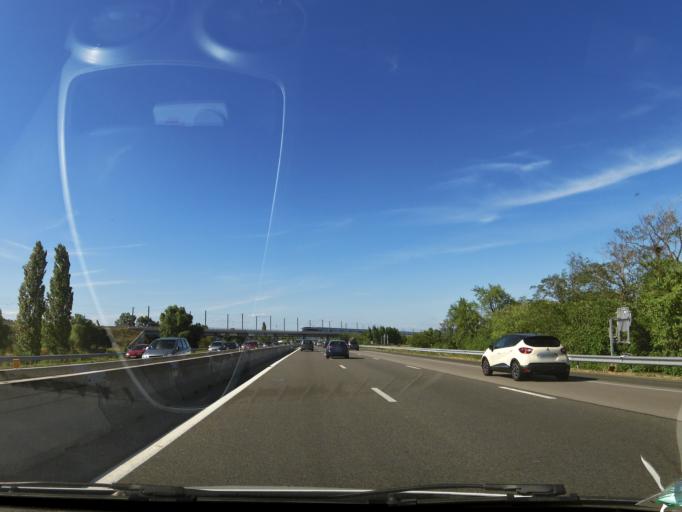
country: FR
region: Rhone-Alpes
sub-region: Departement de la Drome
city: Pierrelatte
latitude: 44.3747
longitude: 4.7328
